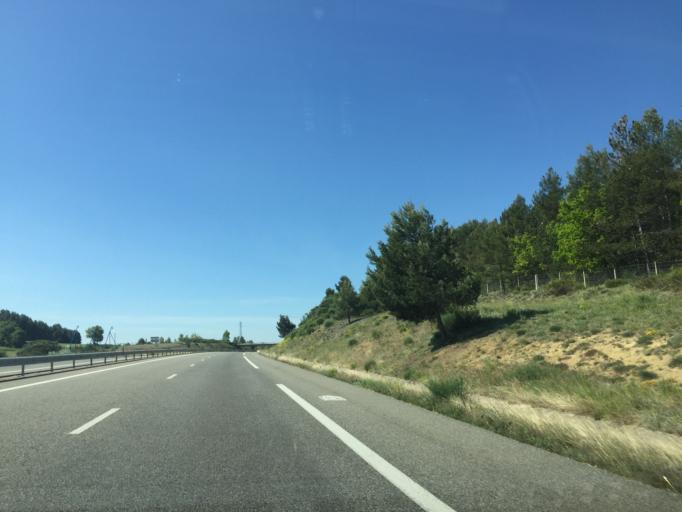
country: FR
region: Provence-Alpes-Cote d'Azur
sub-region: Departement des Alpes-de-Haute-Provence
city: Volonne
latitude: 44.0959
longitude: 5.9933
